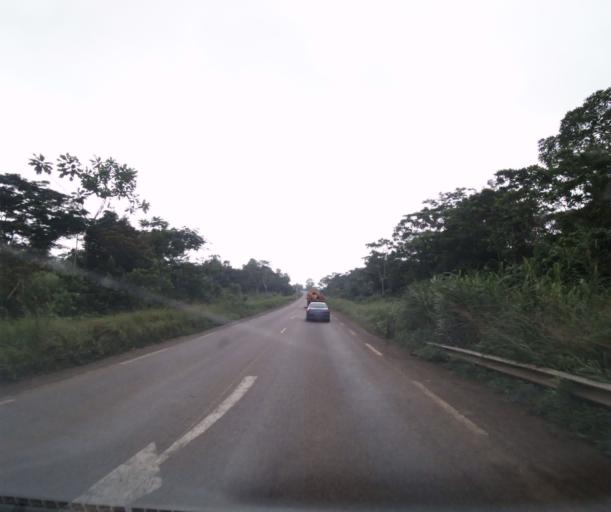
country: CM
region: Littoral
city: Edea
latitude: 3.7928
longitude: 10.2118
